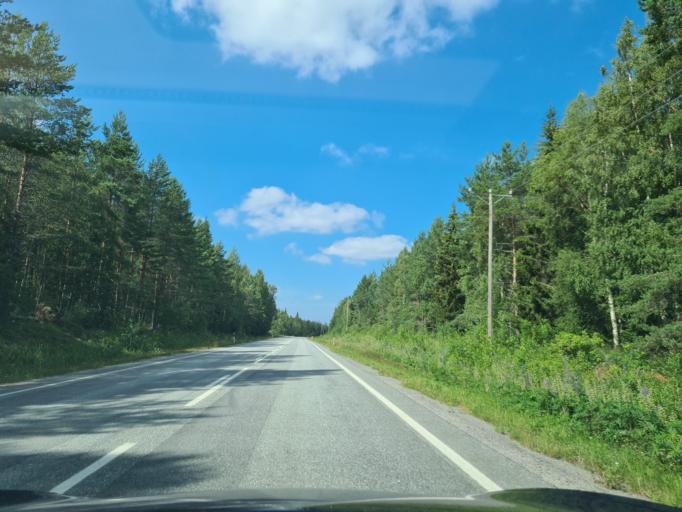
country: FI
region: Ostrobothnia
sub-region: Vaasa
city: Vaasa
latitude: 63.1806
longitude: 21.5727
